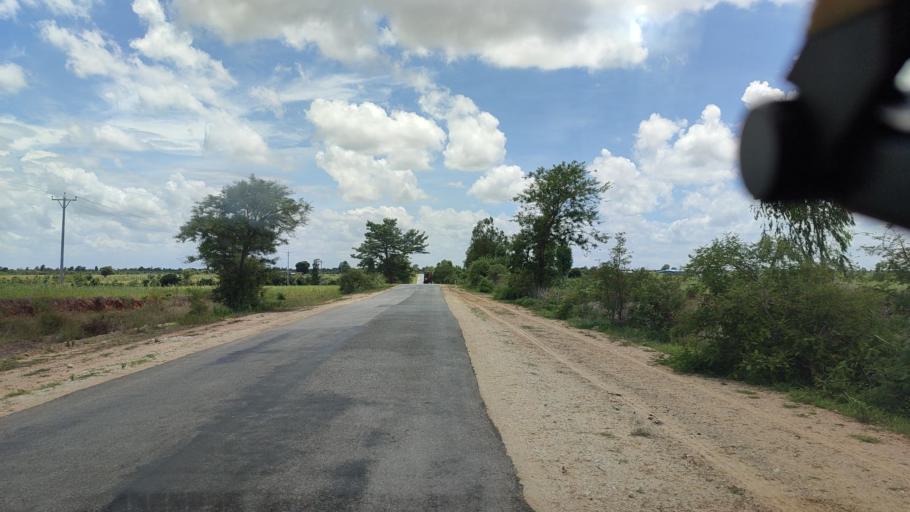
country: MM
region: Magway
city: Taungdwingyi
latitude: 20.2022
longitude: 95.3462
